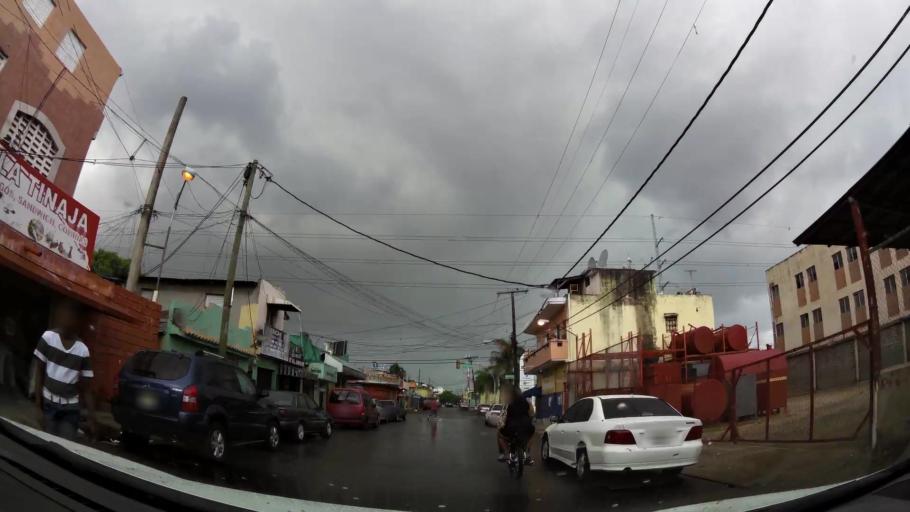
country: DO
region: Nacional
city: Ensanche Luperon
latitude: 18.4942
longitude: -69.9080
